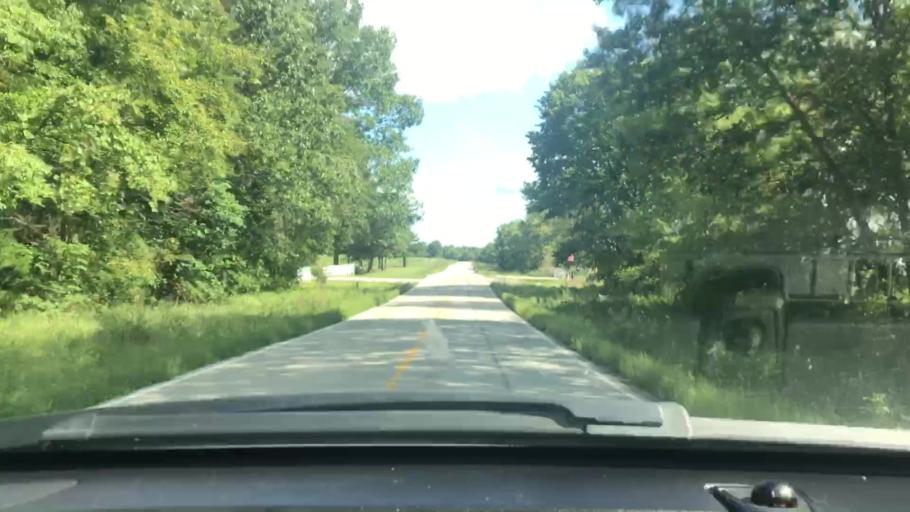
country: US
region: Missouri
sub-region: Wright County
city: Hartville
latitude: 37.3818
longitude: -92.4384
